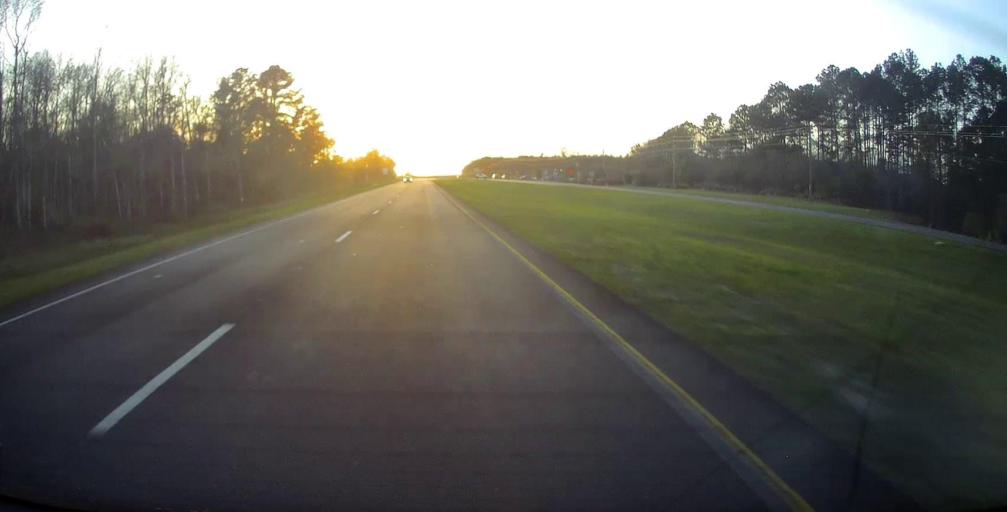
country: US
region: Georgia
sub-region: Chatham County
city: Pooler
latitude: 32.1623
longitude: -81.2526
